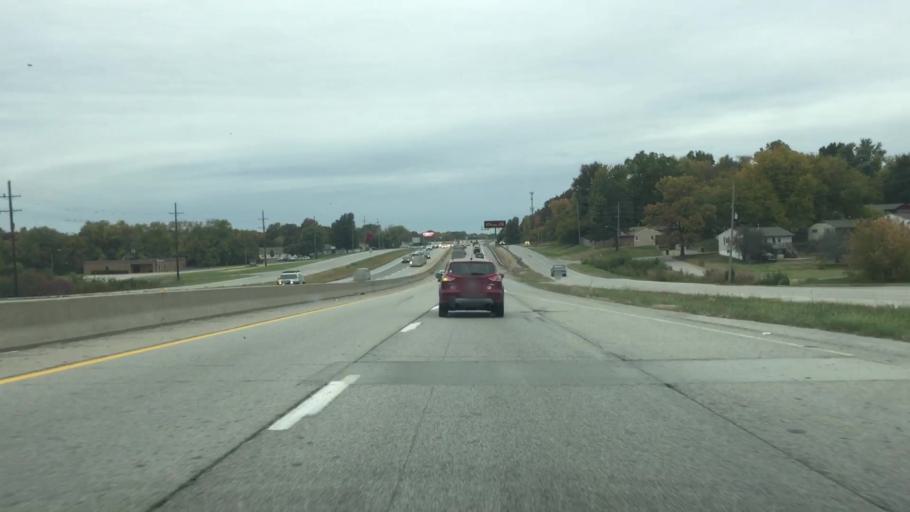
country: US
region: Missouri
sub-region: Jackson County
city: Lees Summit
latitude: 38.9051
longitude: -94.3824
